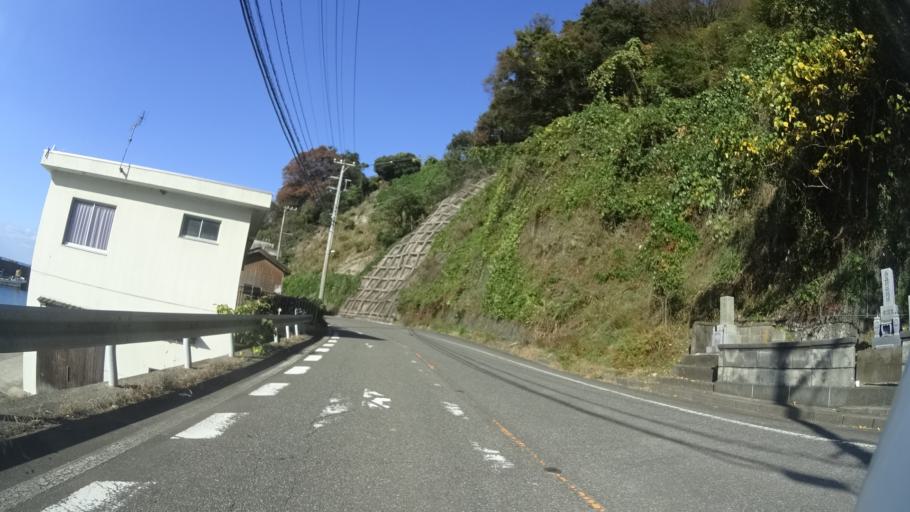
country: JP
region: Fukui
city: Takefu
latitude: 35.8251
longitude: 136.0704
